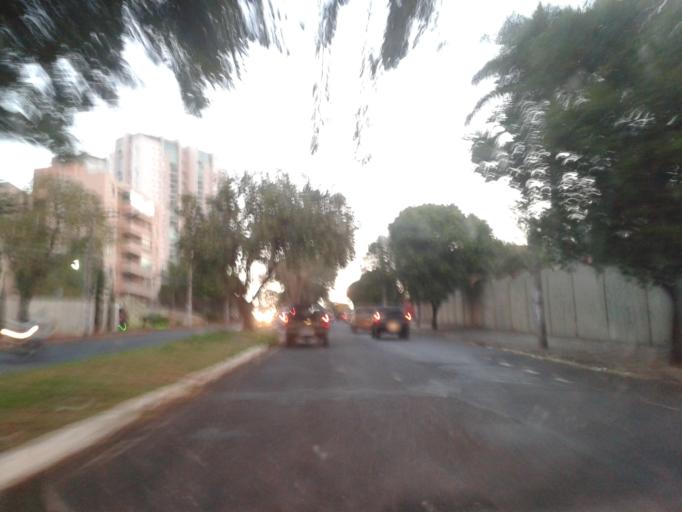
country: BR
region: Minas Gerais
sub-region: Uberlandia
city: Uberlandia
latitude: -18.9286
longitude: -48.2989
